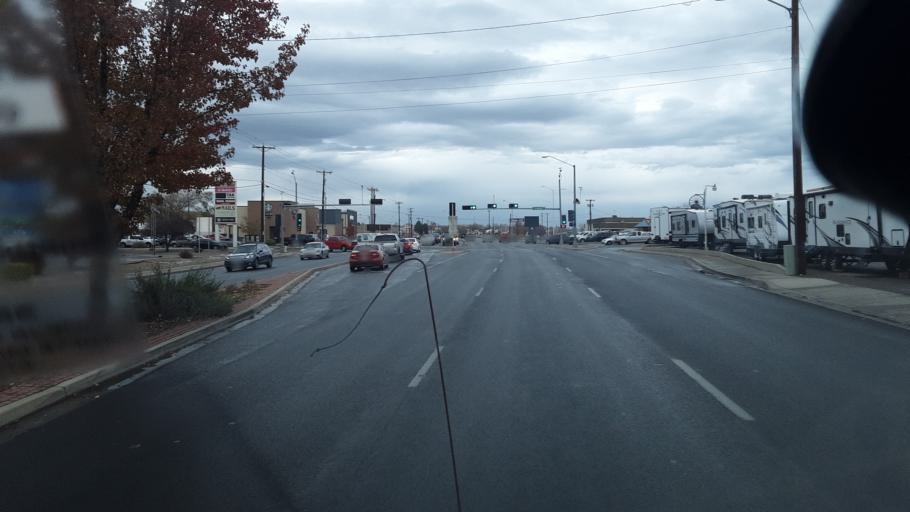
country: US
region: New Mexico
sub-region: San Juan County
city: Farmington
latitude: 36.7421
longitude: -108.1687
